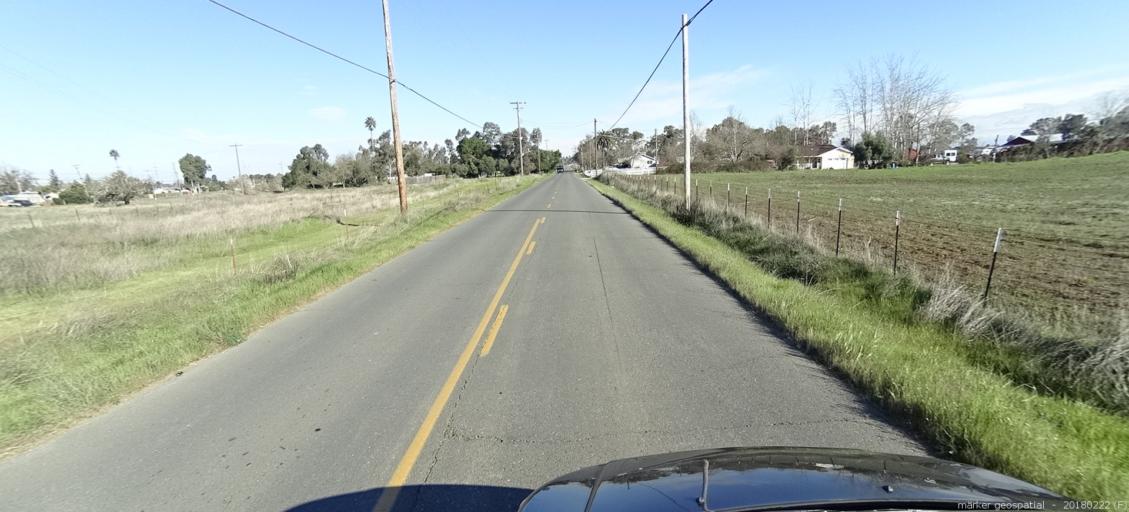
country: US
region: California
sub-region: Sacramento County
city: Elverta
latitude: 38.7220
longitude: -121.4668
